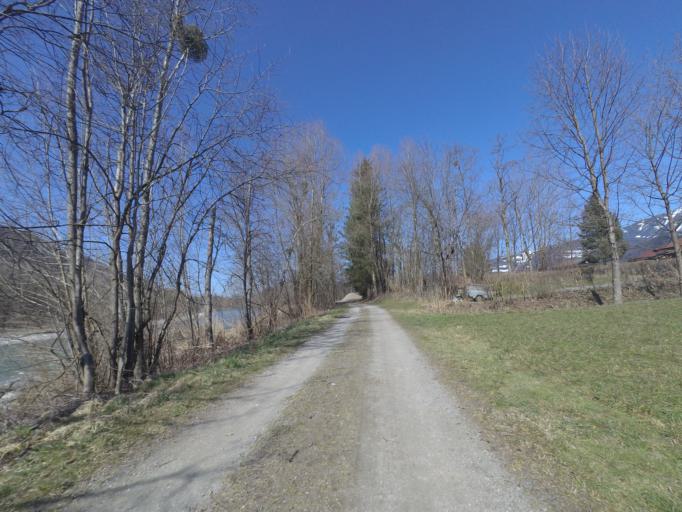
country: AT
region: Salzburg
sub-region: Politischer Bezirk Hallein
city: Kuchl
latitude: 47.6406
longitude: 13.1310
